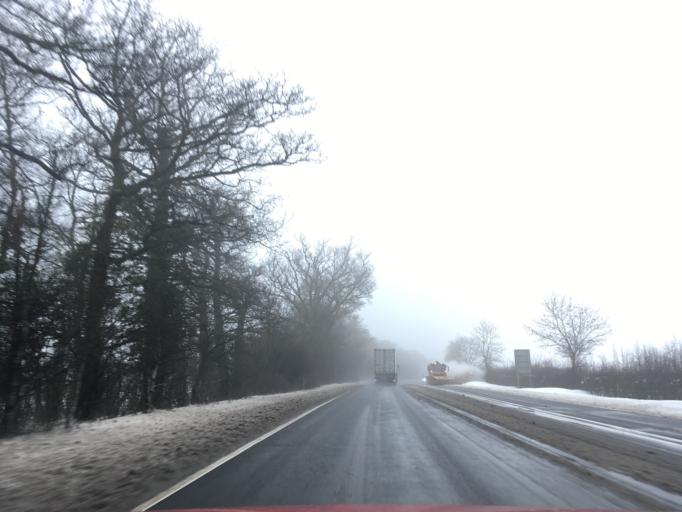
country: GB
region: England
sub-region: Warwickshire
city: Stratford-upon-Avon
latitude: 52.2207
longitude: -1.7085
